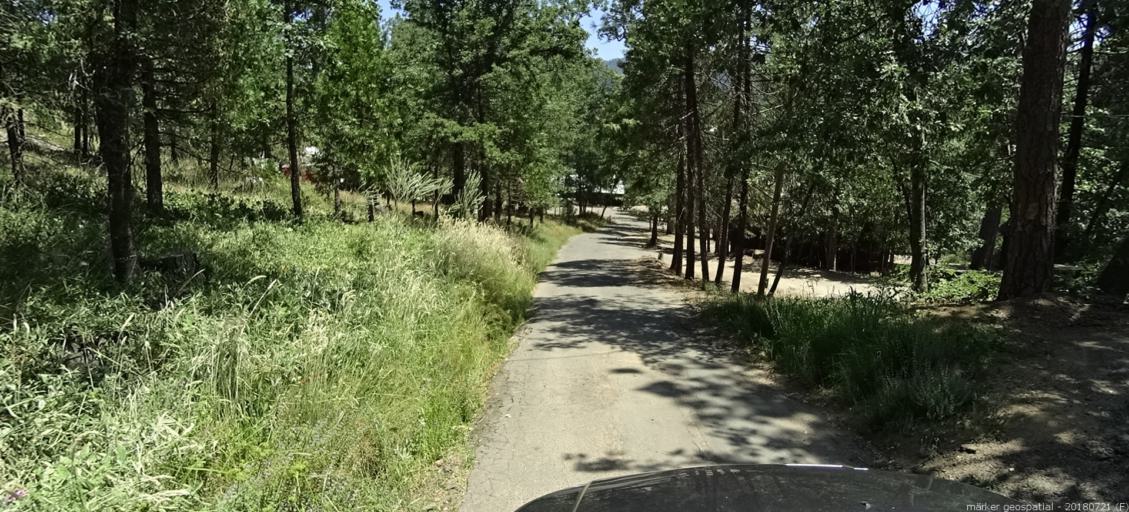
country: US
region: California
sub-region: Madera County
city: Oakhurst
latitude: 37.2978
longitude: -119.5406
